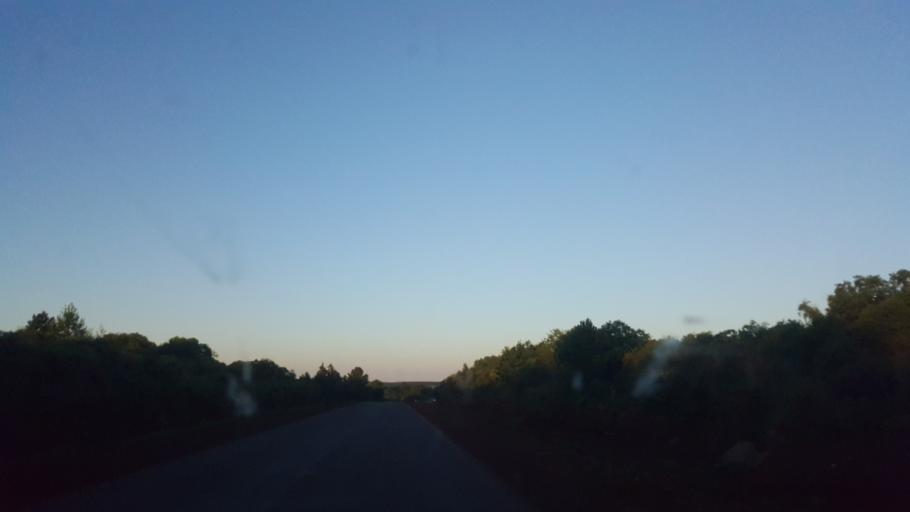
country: AR
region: Corrientes
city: Santo Tome
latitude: -28.4009
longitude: -55.9759
